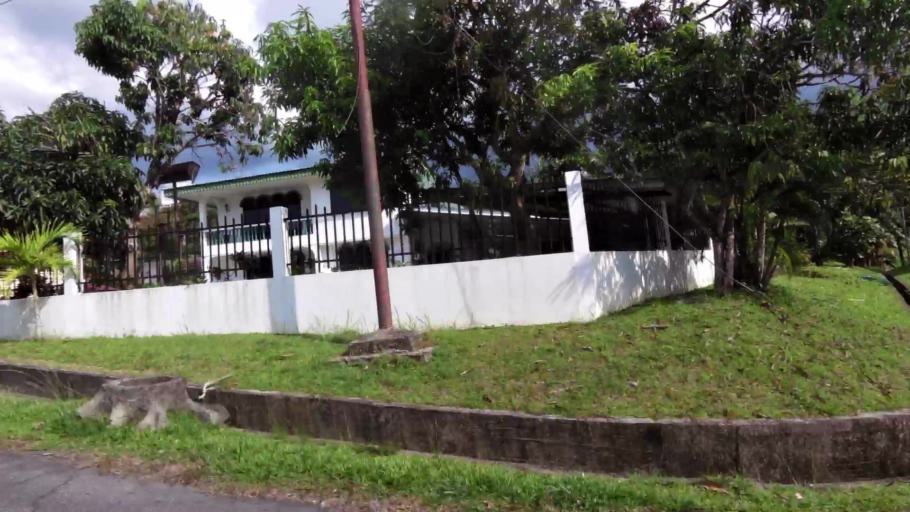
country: BN
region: Brunei and Muara
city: Bandar Seri Begawan
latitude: 4.9604
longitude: 114.9701
